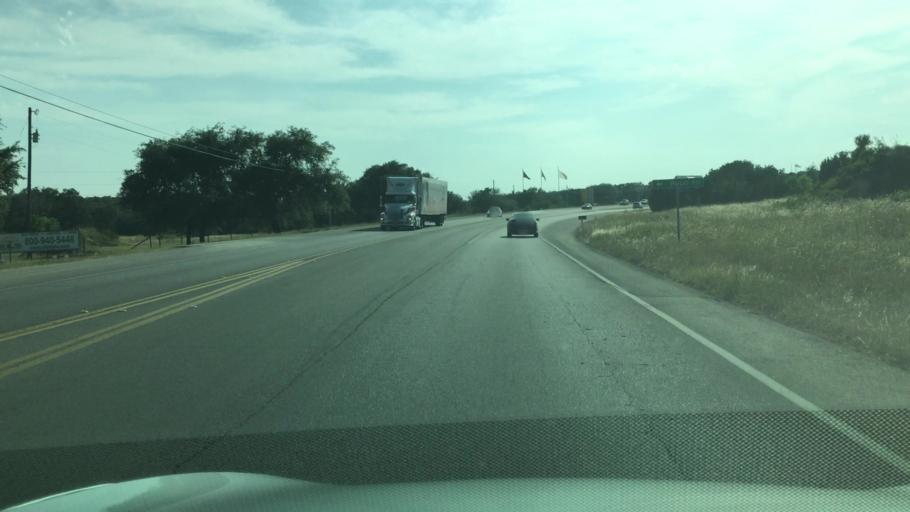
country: US
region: Texas
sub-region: Hays County
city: Wimberley
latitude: 29.9168
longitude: -98.0465
